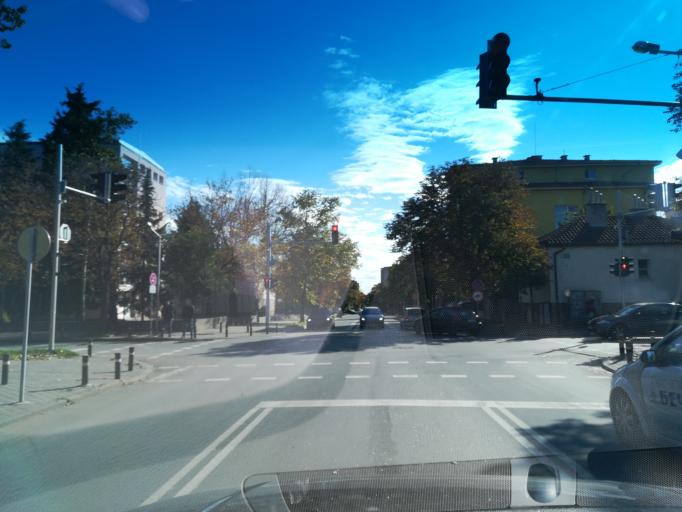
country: BG
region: Stara Zagora
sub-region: Obshtina Stara Zagora
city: Stara Zagora
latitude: 42.4306
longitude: 25.6399
